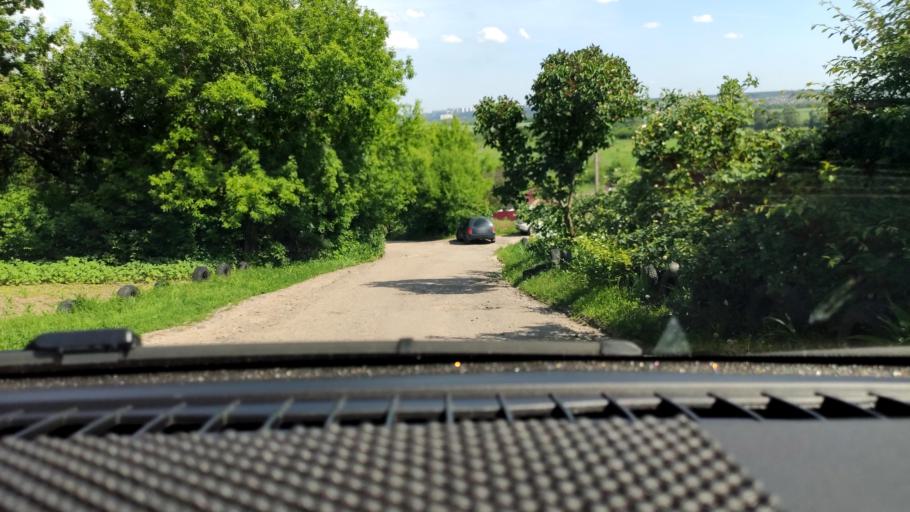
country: RU
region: Voronezj
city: Semiluki
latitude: 51.7255
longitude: 39.0470
